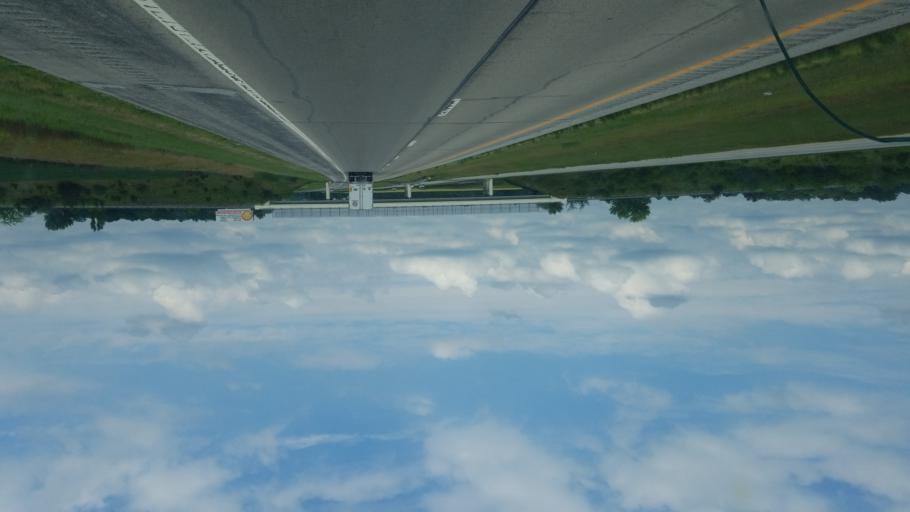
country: US
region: Ohio
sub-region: Allen County
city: Elida
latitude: 40.8348
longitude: -84.1688
